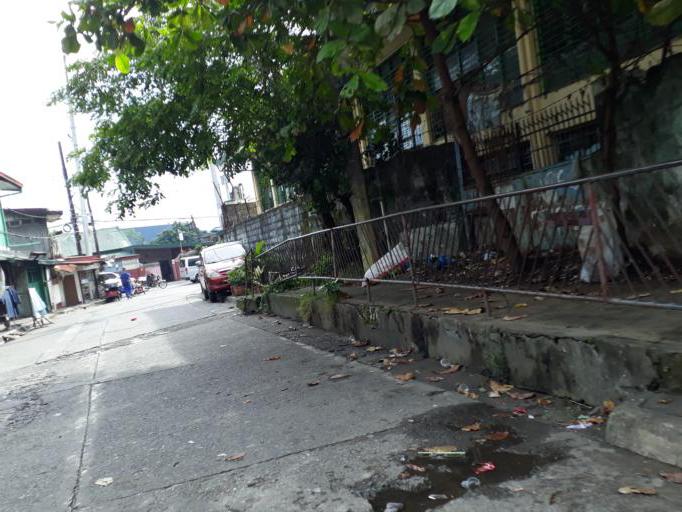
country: PH
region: Calabarzon
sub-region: Province of Rizal
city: Valenzuela
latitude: 14.6751
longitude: 120.9849
